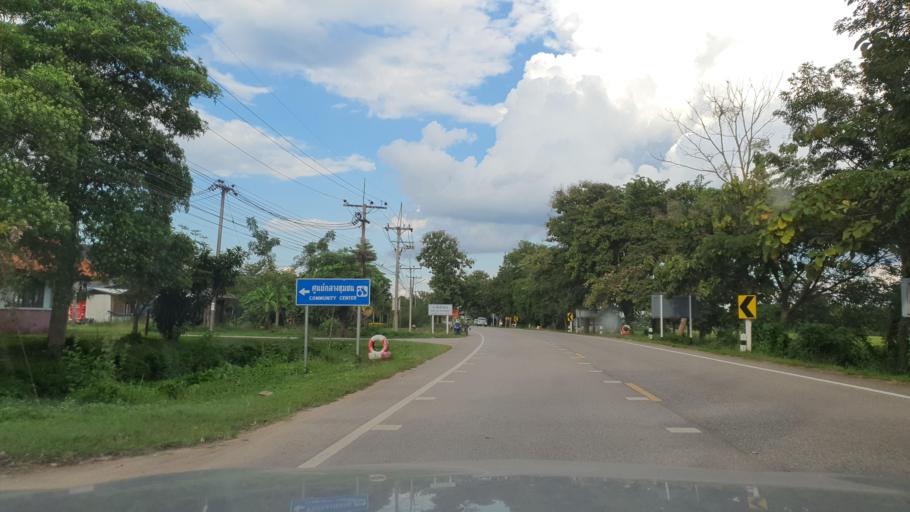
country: TH
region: Phayao
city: Phayao
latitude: 19.1760
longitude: 99.8344
